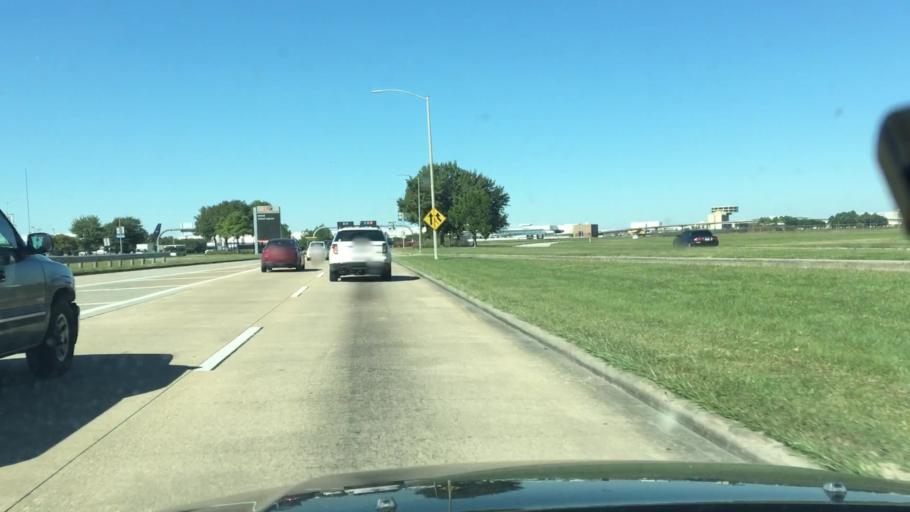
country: US
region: Texas
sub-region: Harris County
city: Aldine
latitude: 29.9735
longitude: -95.3407
